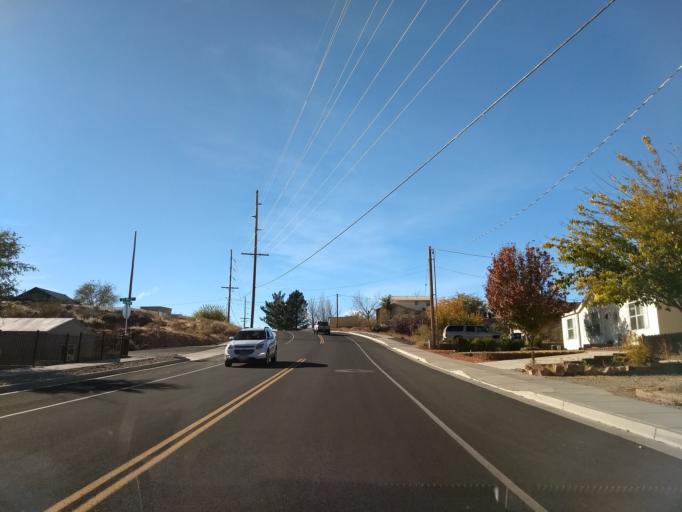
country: US
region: Utah
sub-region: Washington County
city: Hurricane
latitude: 37.1857
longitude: -113.2888
